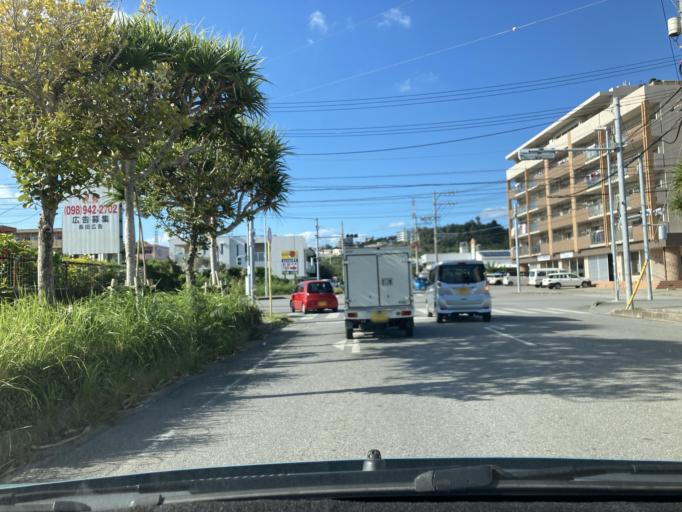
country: JP
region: Okinawa
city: Okinawa
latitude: 26.3348
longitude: 127.8373
